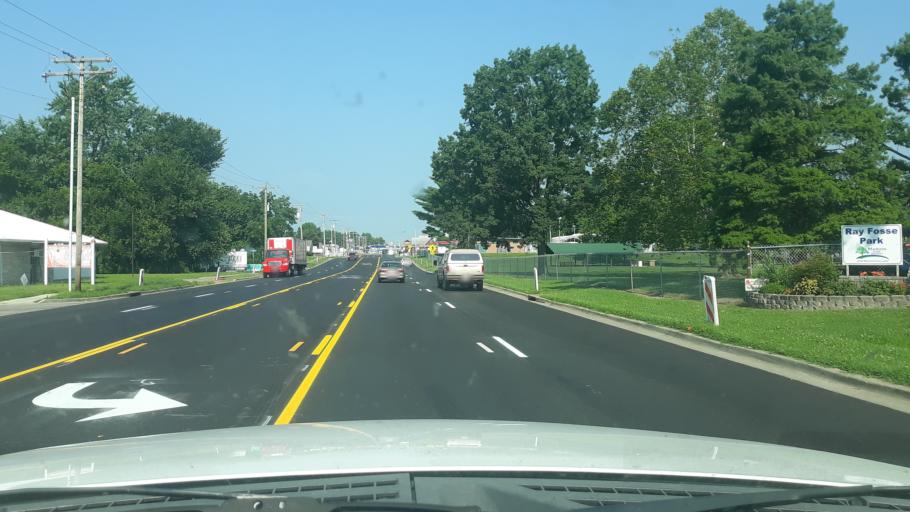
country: US
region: Illinois
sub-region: Williamson County
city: Marion
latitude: 37.7406
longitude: -88.9183
